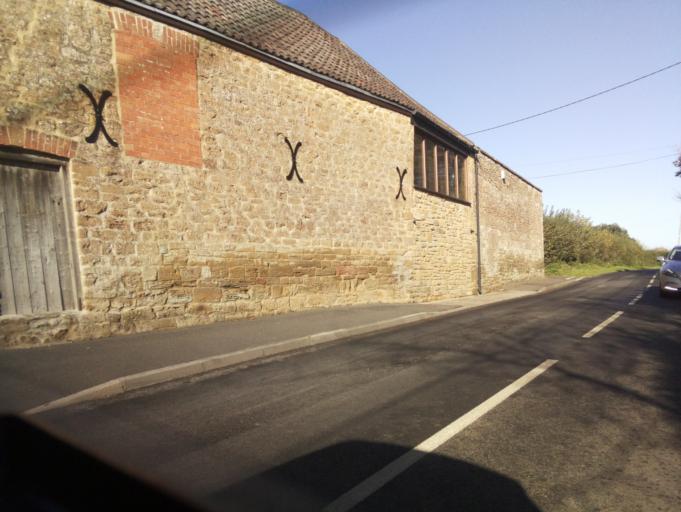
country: GB
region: England
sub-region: Somerset
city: Martock
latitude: 50.9861
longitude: -2.7662
